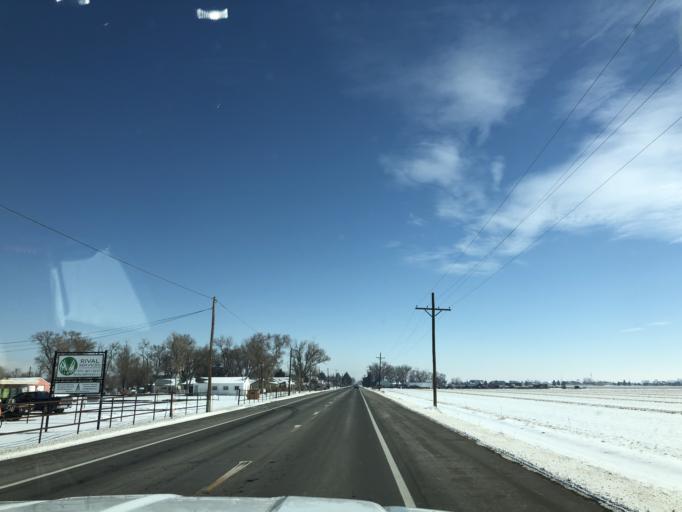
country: US
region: Colorado
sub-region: Morgan County
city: Fort Morgan
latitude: 40.2541
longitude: -103.8579
